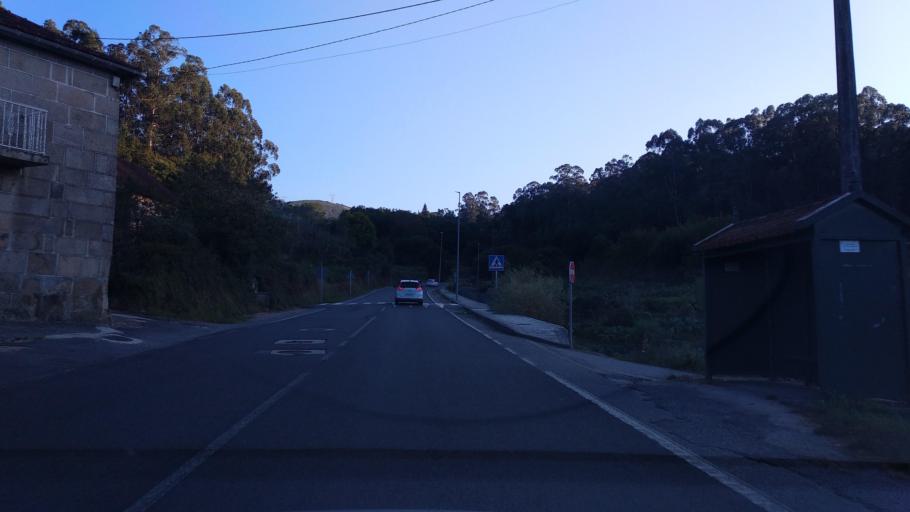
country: ES
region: Galicia
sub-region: Provincia de Pontevedra
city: Redondela
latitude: 42.3356
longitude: -8.5798
